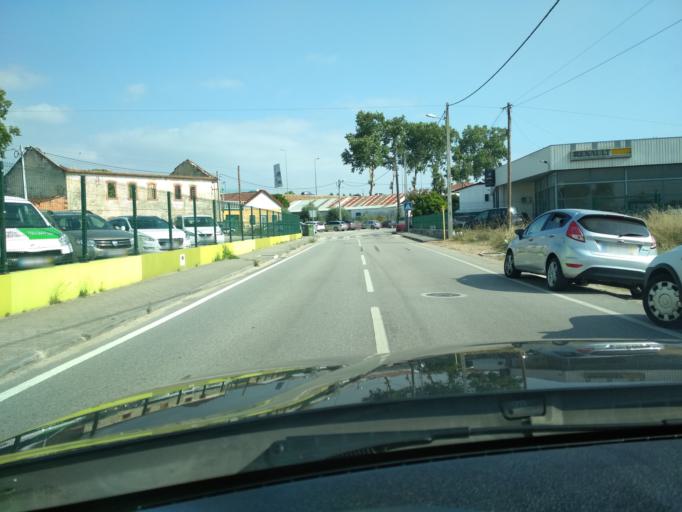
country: PT
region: Aveiro
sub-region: Mealhada
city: Mealhada
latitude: 40.3705
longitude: -8.4546
